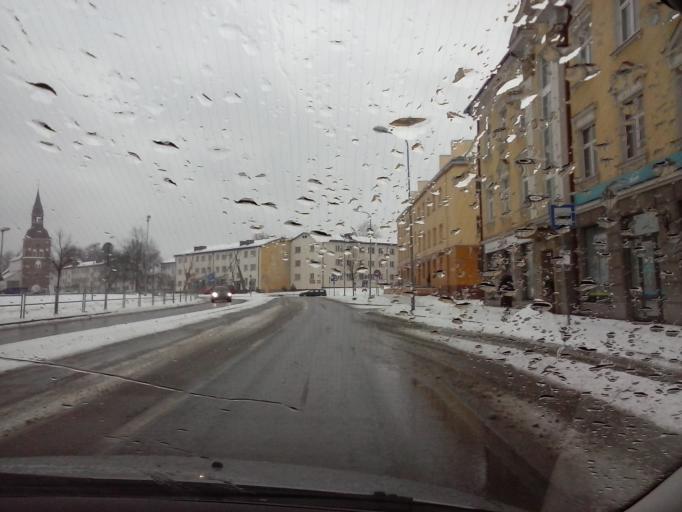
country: LV
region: Valmieras Rajons
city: Valmiera
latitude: 57.5382
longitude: 25.4213
